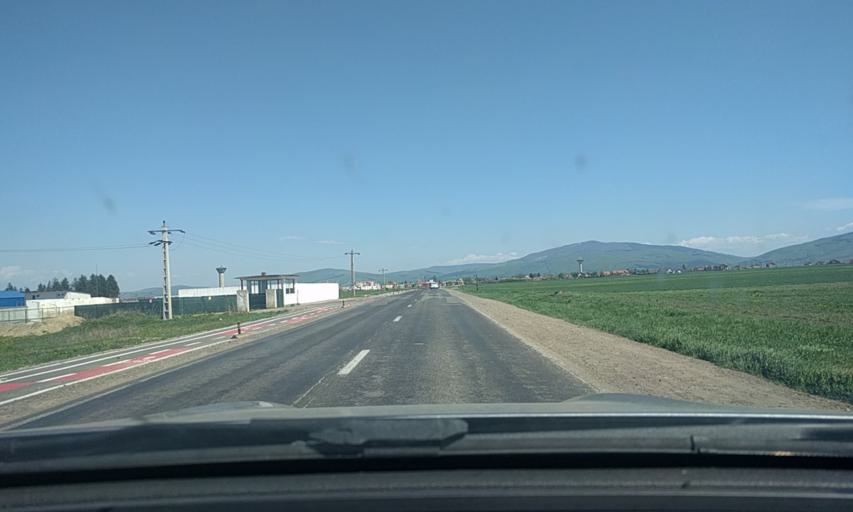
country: RO
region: Brasov
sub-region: Comuna Prejmer
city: Prejmer
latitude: 45.7163
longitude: 25.7505
